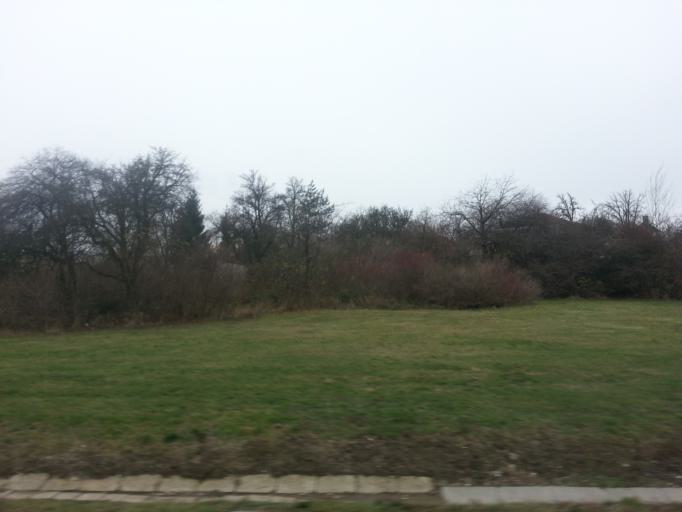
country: CZ
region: Central Bohemia
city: Tuchomerice
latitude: 50.1014
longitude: 14.2896
